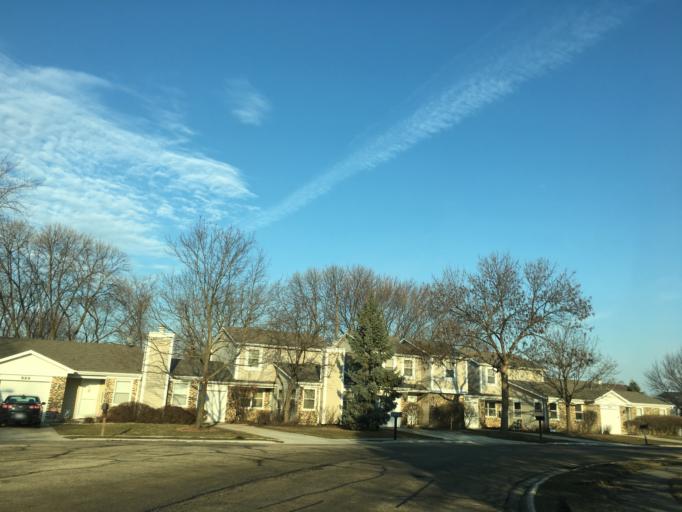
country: US
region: Illinois
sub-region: Cook County
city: Schaumburg
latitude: 42.0422
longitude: -88.1036
